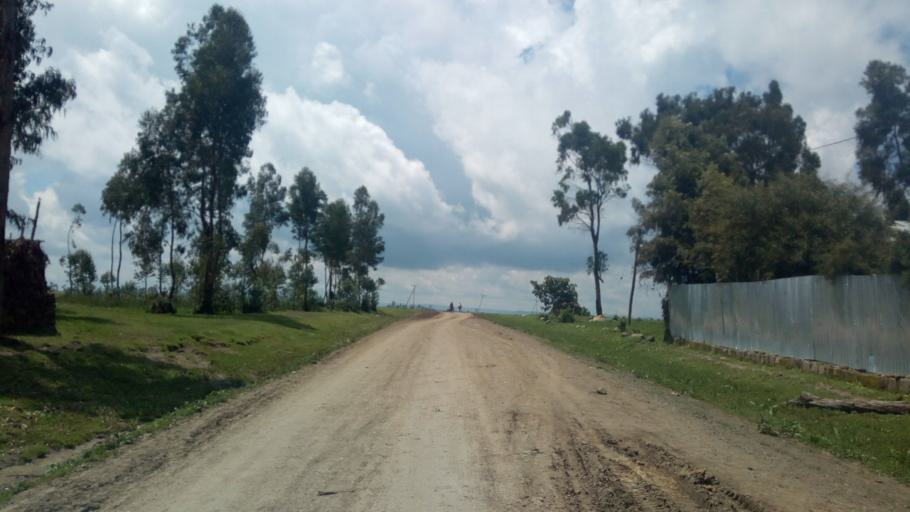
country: ET
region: Oromiya
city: Sendafa
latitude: 9.0014
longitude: 39.1265
